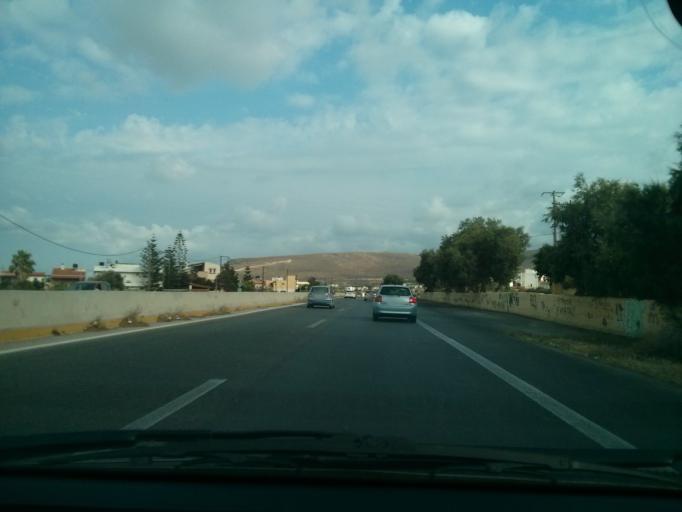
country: GR
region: Crete
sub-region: Nomos Irakleiou
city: Kokkini Hani
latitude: 35.3291
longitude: 25.2473
